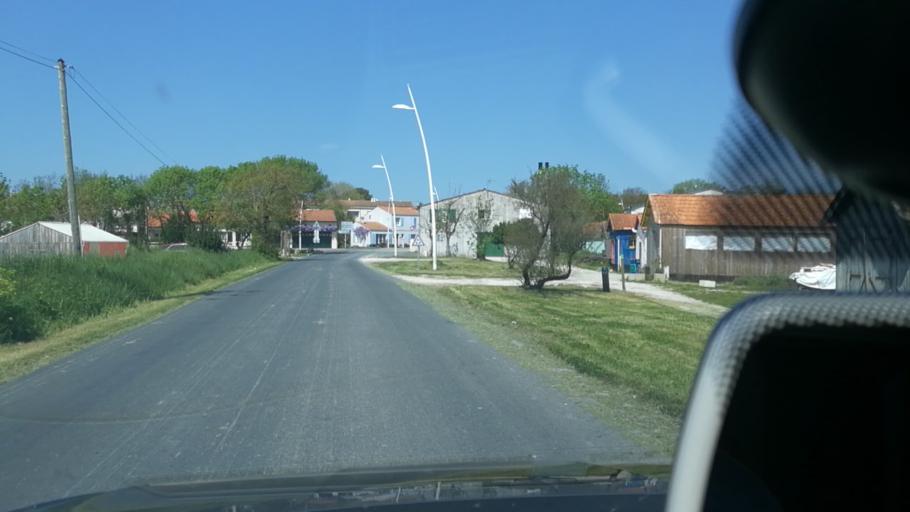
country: FR
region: Poitou-Charentes
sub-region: Departement de la Charente-Maritime
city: Saint-Trojan-les-Bains
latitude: 45.8830
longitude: -1.1956
